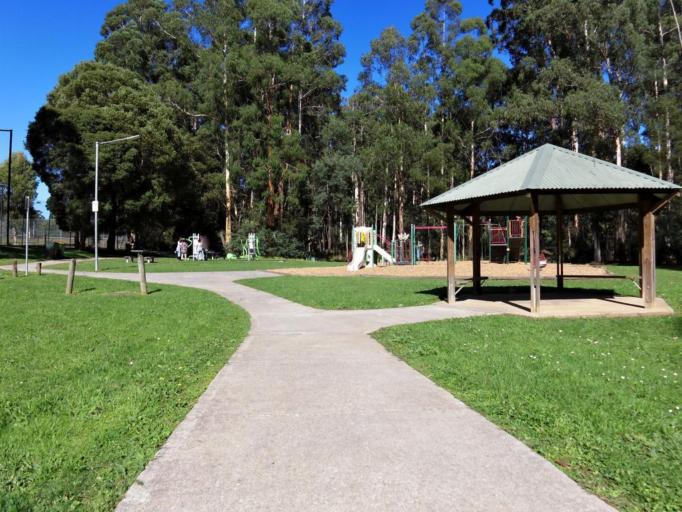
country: AU
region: Victoria
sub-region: Cardinia
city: Cockatoo
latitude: -37.9365
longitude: 145.4896
